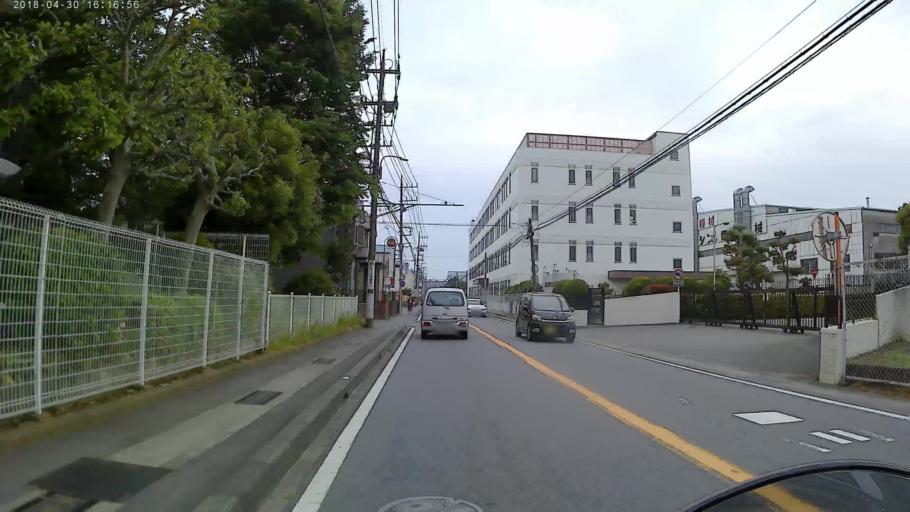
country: JP
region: Kanagawa
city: Minami-rinkan
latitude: 35.4818
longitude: 139.4317
